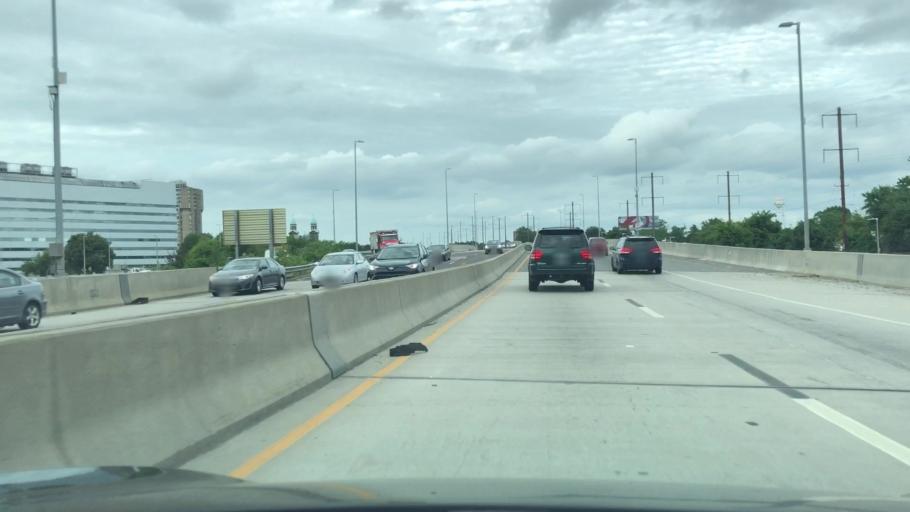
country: US
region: Pennsylvania
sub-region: Bucks County
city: Morrisville
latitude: 40.2097
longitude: -74.7662
